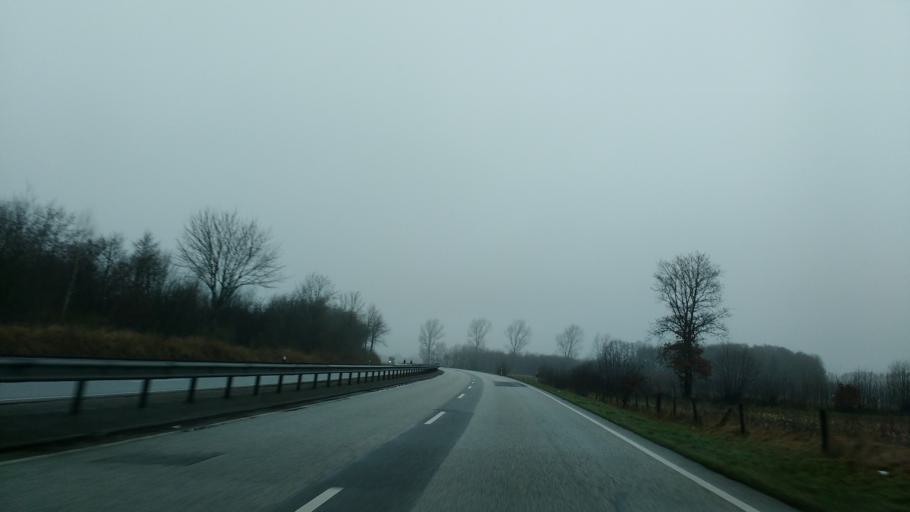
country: DE
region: Schleswig-Holstein
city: Jevenstedt
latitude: 54.2388
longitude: 9.6768
